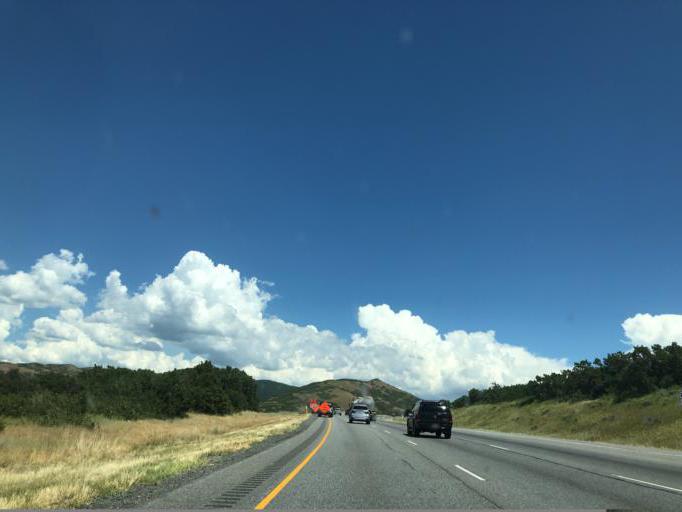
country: US
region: Utah
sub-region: Summit County
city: Summit Park
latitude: 40.7483
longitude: -111.7070
